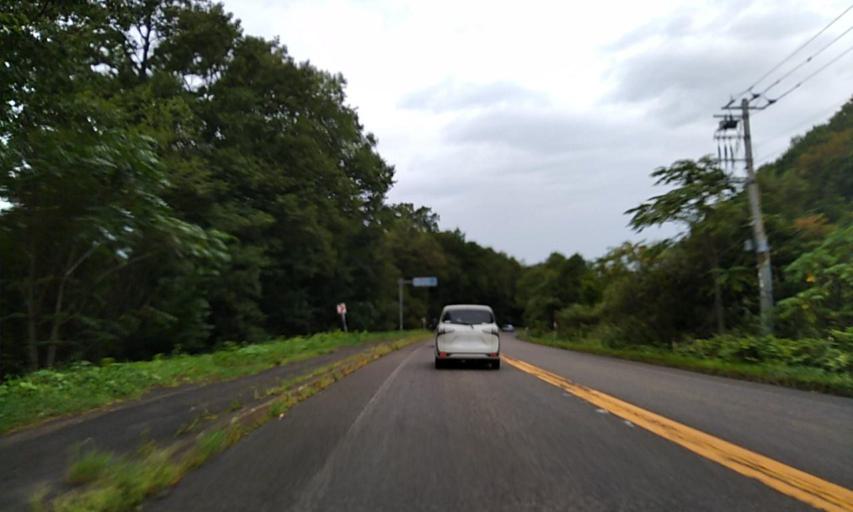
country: JP
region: Hokkaido
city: Abashiri
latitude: 43.9759
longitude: 144.2171
